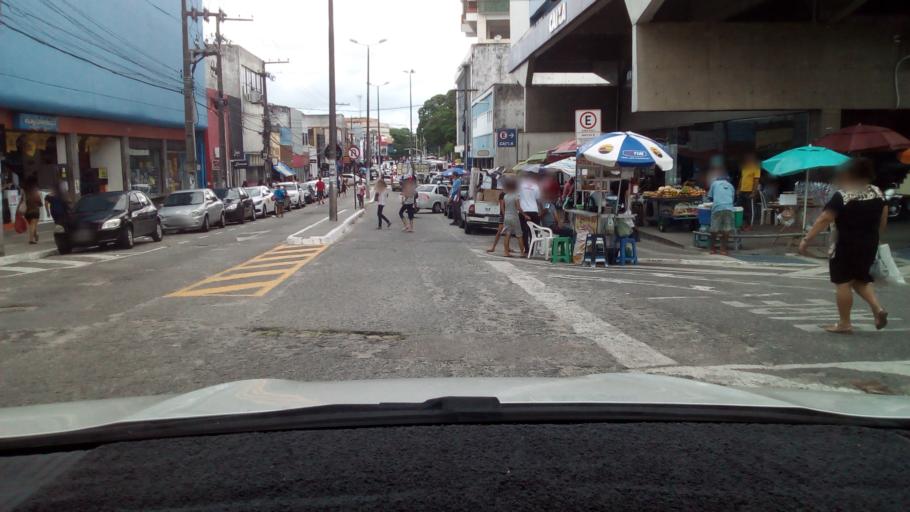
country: BR
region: Paraiba
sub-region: Joao Pessoa
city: Joao Pessoa
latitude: -7.1179
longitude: -34.8821
